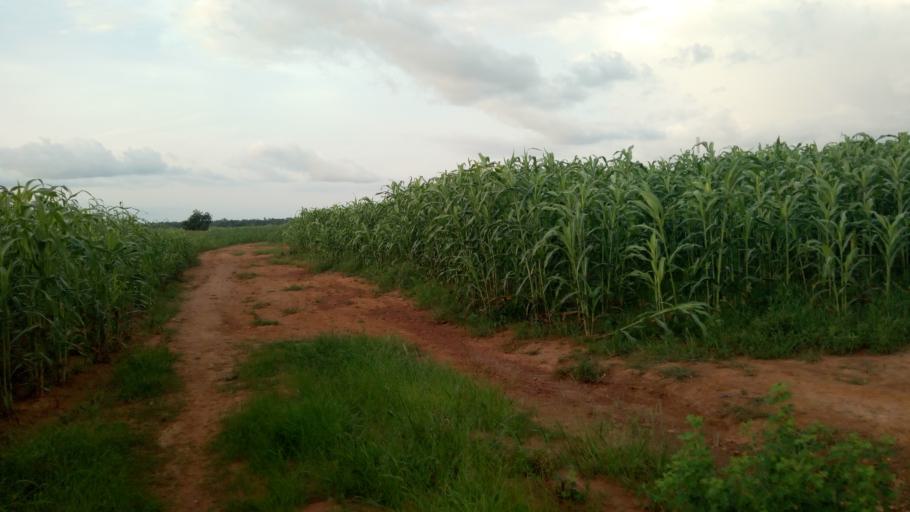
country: ML
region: Sikasso
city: Koutiala
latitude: 12.3763
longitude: -5.4983
